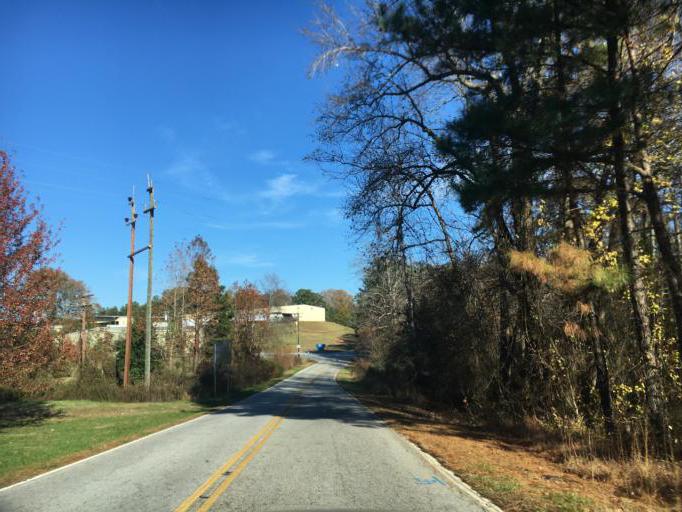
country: US
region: South Carolina
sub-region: Spartanburg County
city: Southern Shops
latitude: 35.0003
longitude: -82.0482
